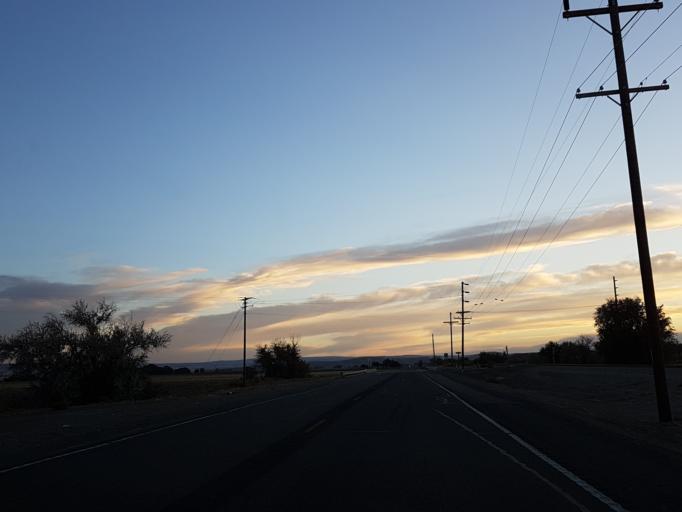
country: US
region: Oregon
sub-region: Malheur County
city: Vale
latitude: 43.9684
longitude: -117.2707
